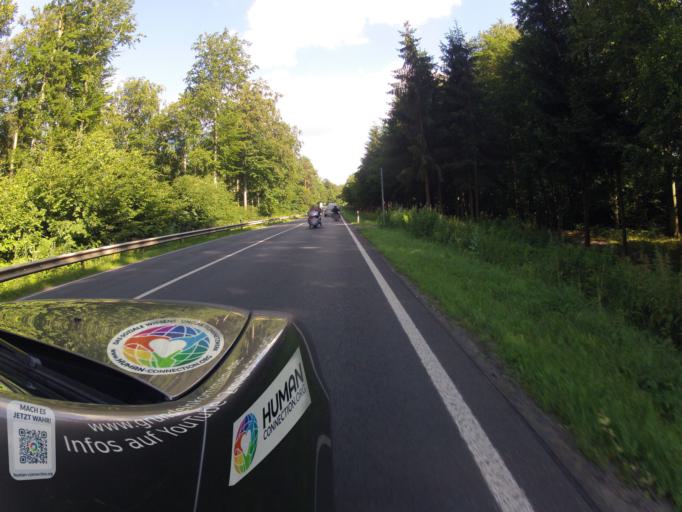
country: DE
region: Mecklenburg-Vorpommern
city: Seebad Bansin
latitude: 53.9739
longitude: 14.1135
